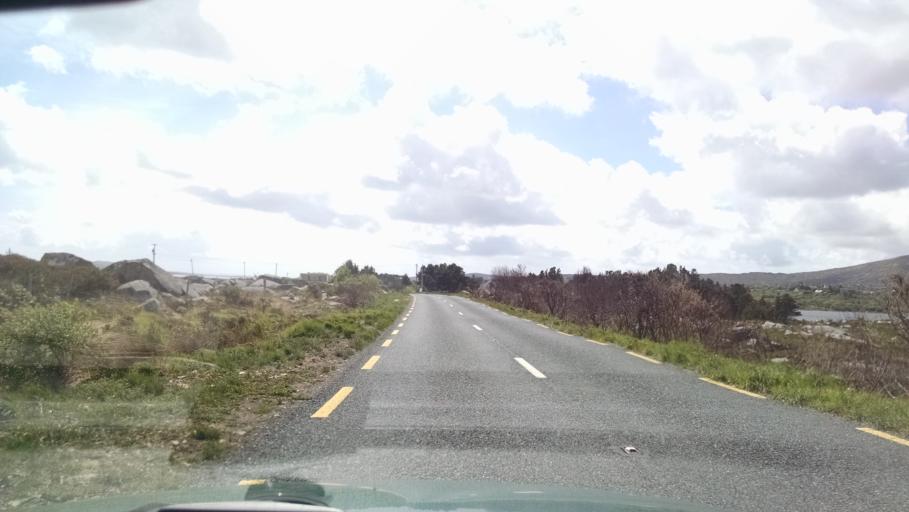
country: IE
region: Connaught
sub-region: County Galway
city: Oughterard
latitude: 53.3730
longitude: -9.6817
